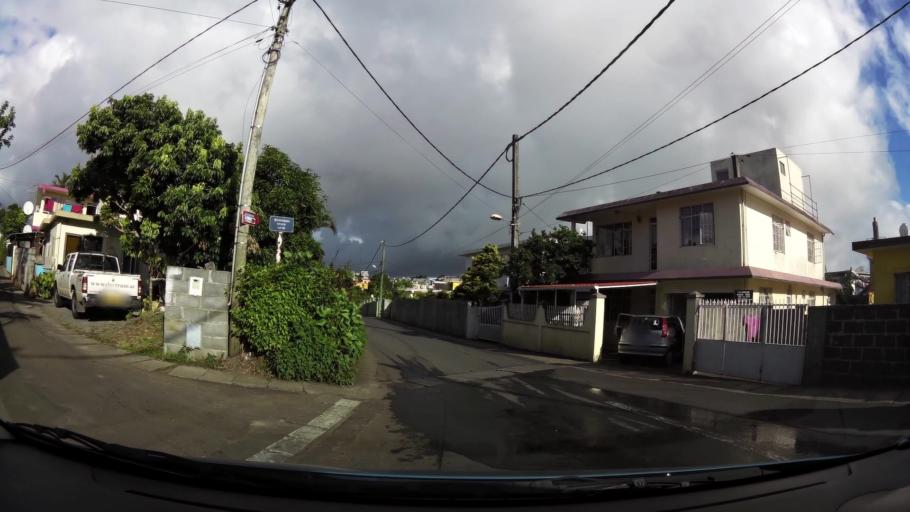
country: MU
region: Plaines Wilhems
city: Curepipe
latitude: -20.3256
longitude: 57.5062
